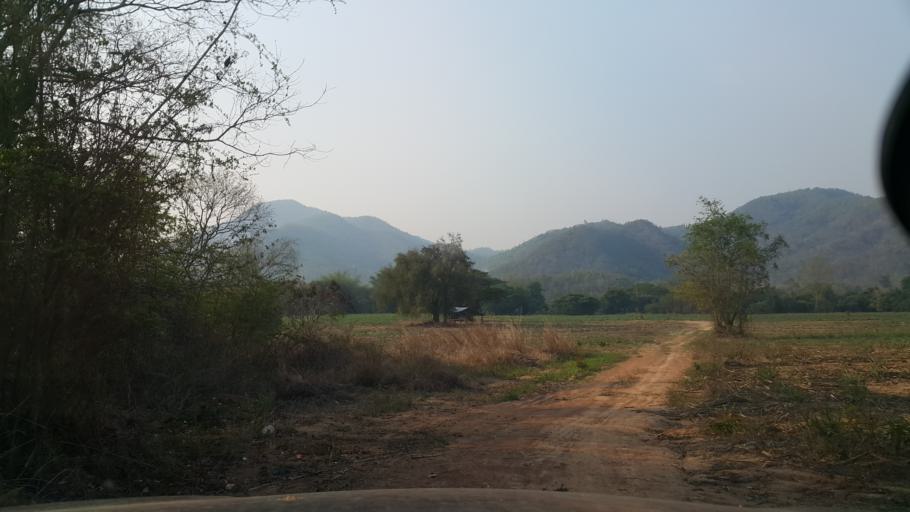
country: TH
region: Sukhothai
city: Thung Saliam
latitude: 17.3382
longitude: 99.4682
